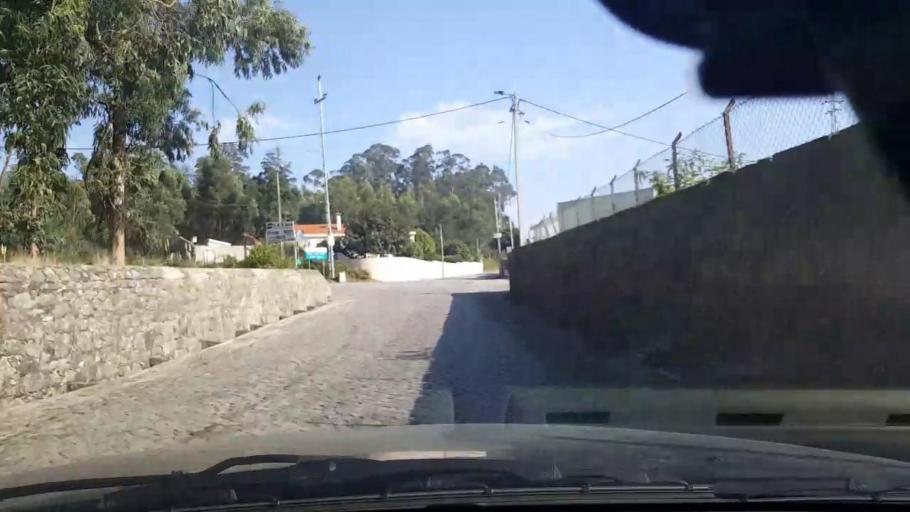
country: PT
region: Porto
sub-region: Maia
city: Gemunde
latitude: 41.2739
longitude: -8.6676
